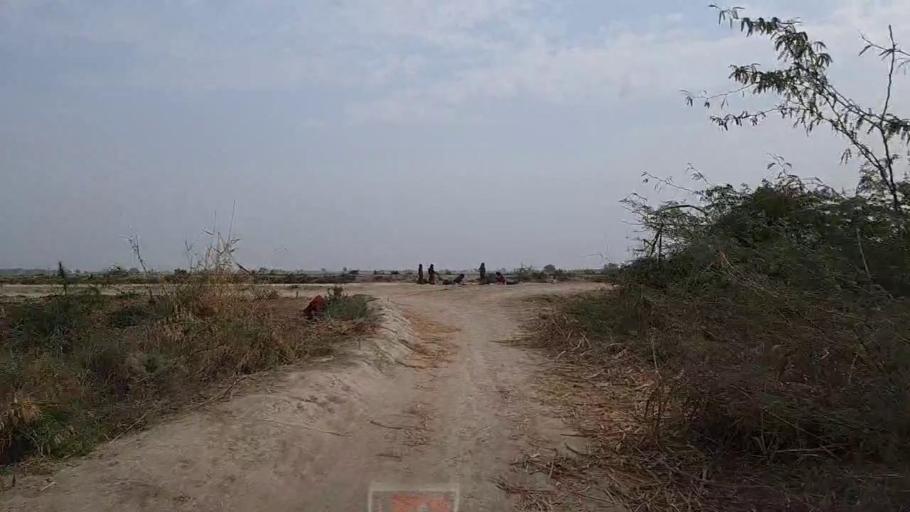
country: PK
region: Sindh
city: Mirwah Gorchani
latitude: 25.3887
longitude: 69.0614
